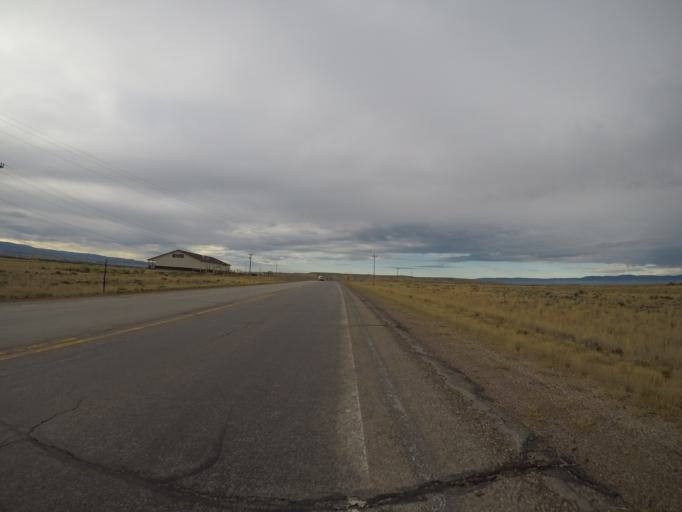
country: US
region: Wyoming
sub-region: Carbon County
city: Saratoga
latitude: 41.4358
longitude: -106.8045
